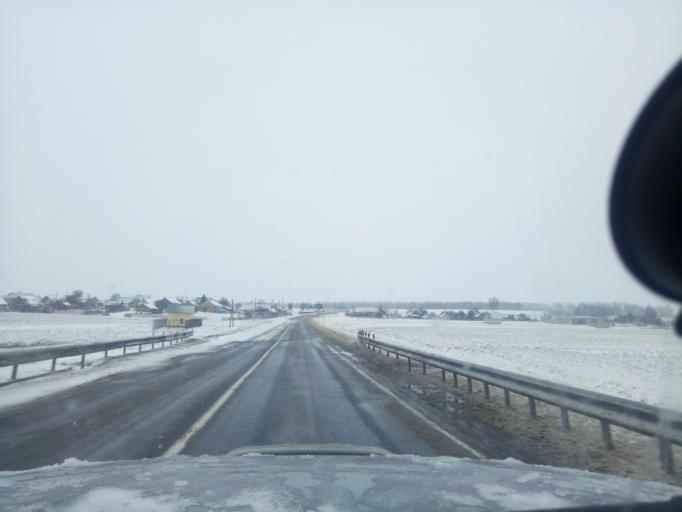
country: BY
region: Minsk
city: Haradzyeya
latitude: 53.3329
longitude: 26.5365
